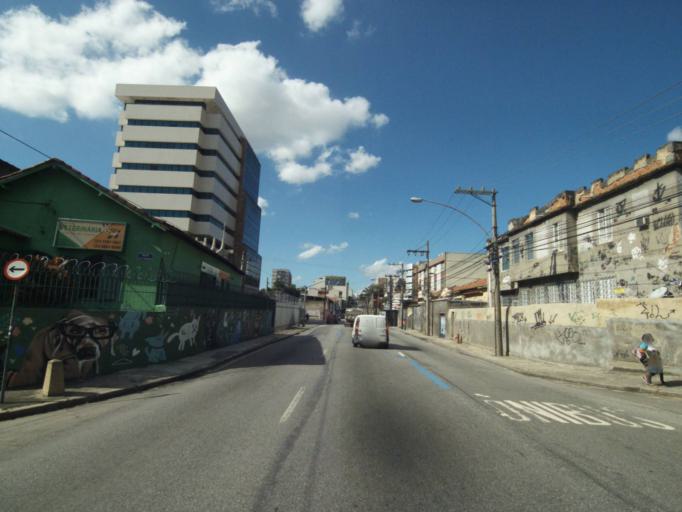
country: BR
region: Rio de Janeiro
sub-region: Rio De Janeiro
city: Rio de Janeiro
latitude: -22.9033
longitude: -43.2540
